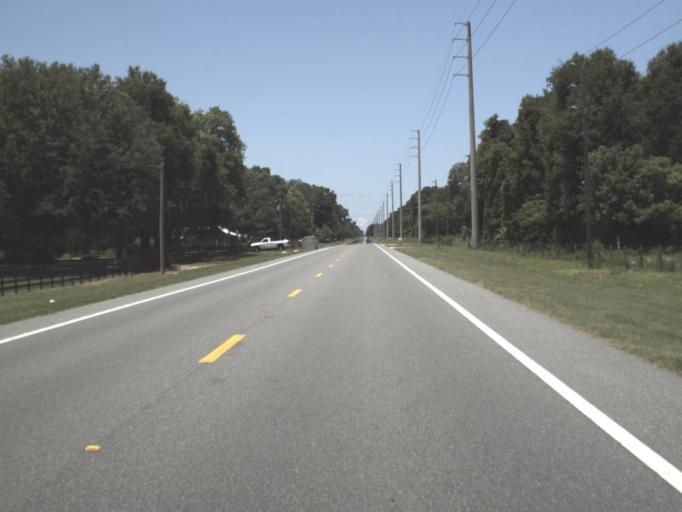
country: US
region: Florida
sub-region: Dixie County
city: Cross City
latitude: 29.6885
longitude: -82.9843
